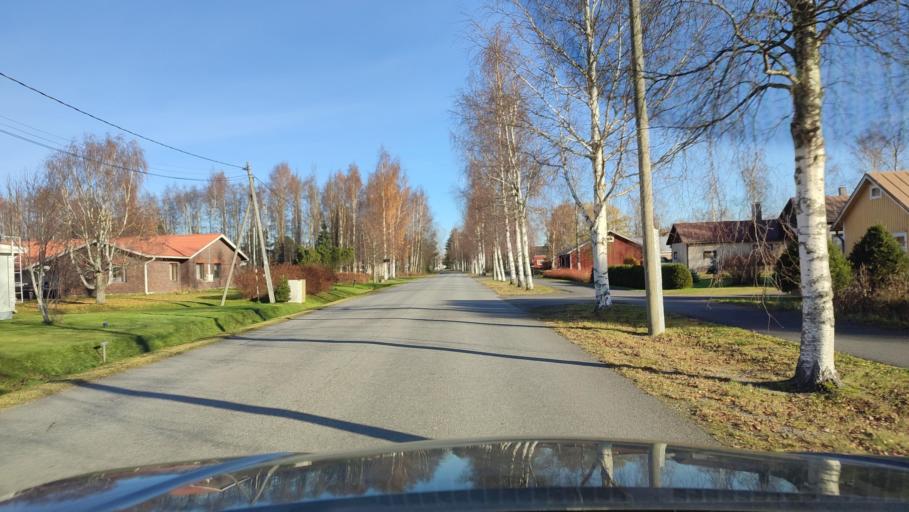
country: FI
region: Southern Ostrobothnia
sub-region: Suupohja
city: Teuva
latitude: 62.4791
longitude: 21.7497
